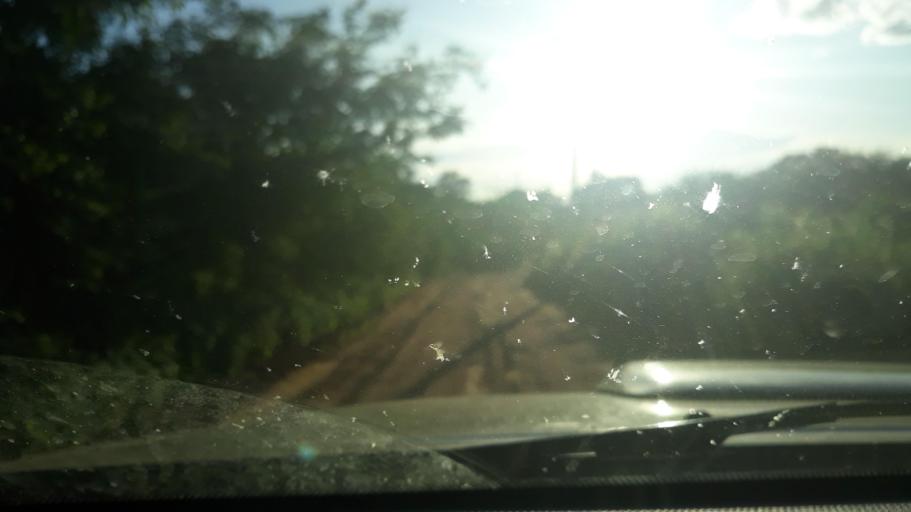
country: BR
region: Bahia
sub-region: Riacho De Santana
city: Riacho de Santana
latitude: -13.8468
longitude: -42.7451
